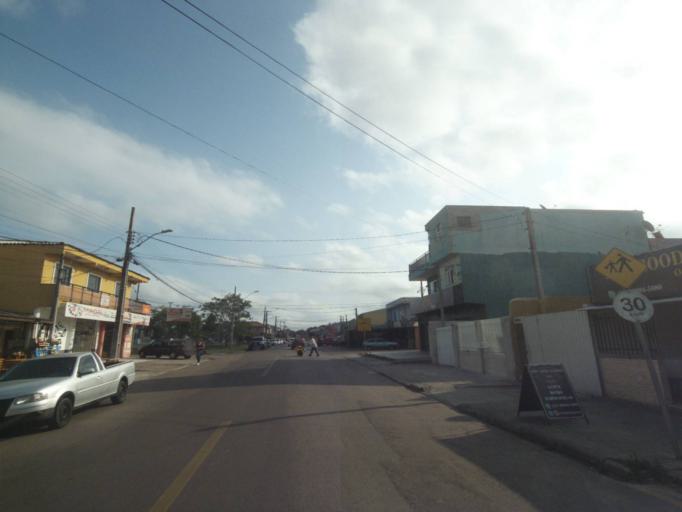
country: BR
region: Parana
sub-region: Sao Jose Dos Pinhais
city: Sao Jose dos Pinhais
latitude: -25.5430
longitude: -49.2576
